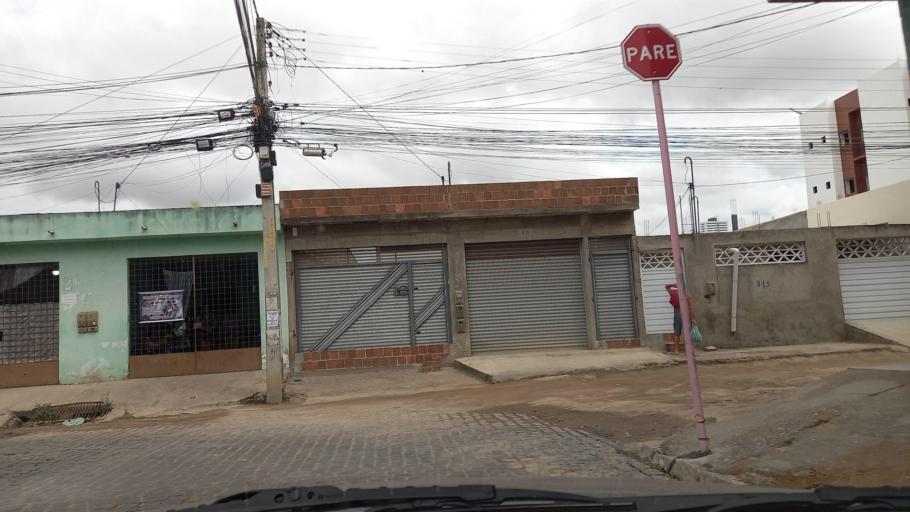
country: BR
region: Pernambuco
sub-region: Caruaru
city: Caruaru
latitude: -8.2700
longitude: -35.9593
